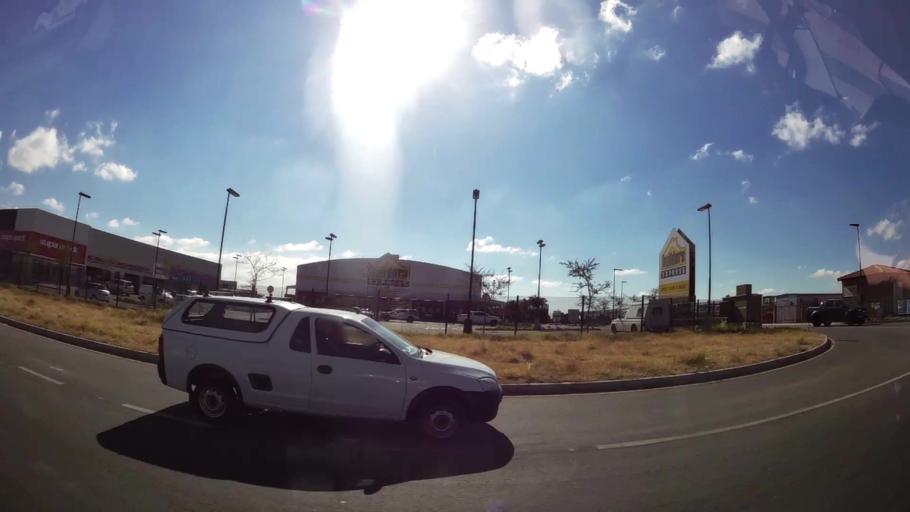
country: ZA
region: Gauteng
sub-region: West Rand District Municipality
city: Krugersdorp
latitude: -26.0837
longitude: 27.8055
